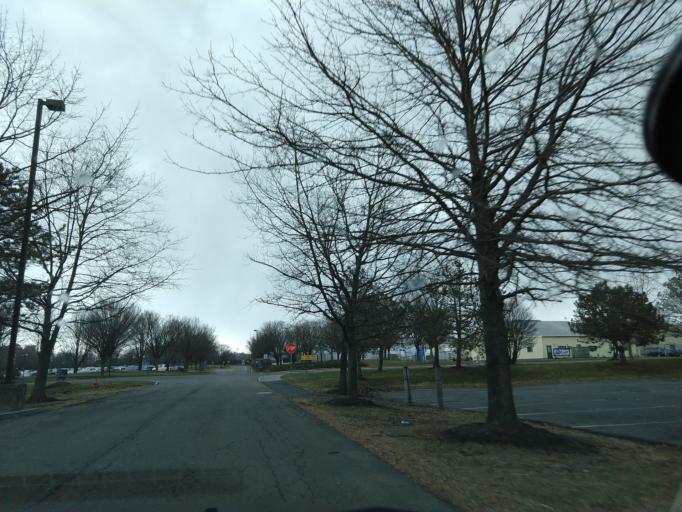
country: US
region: New York
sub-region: Tompkins County
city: Northeast Ithaca
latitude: 42.4870
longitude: -76.4626
